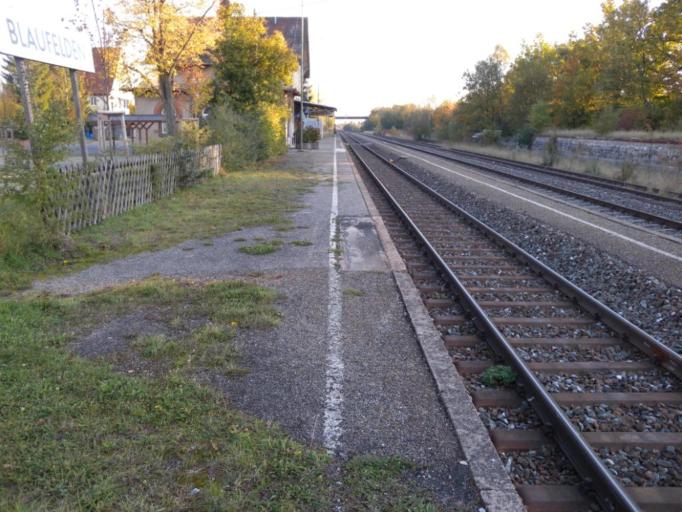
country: DE
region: Baden-Wuerttemberg
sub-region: Regierungsbezirk Stuttgart
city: Blaufelden
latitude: 49.2967
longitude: 9.9675
